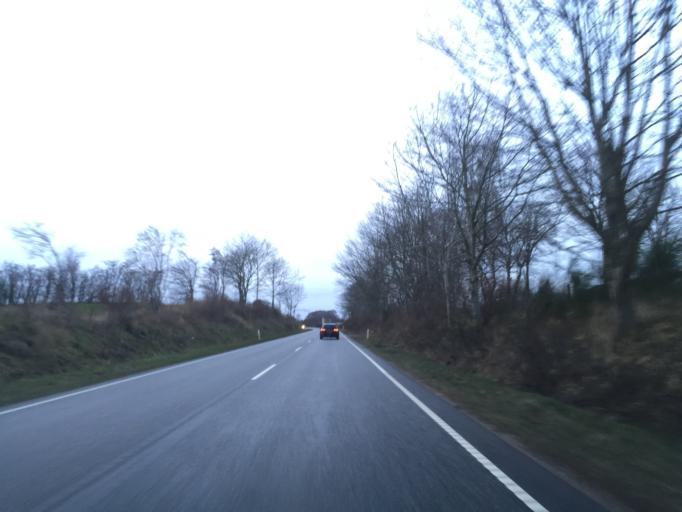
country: DK
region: Central Jutland
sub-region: Viborg Kommune
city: Bjerringbro
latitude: 56.3110
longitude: 9.5575
